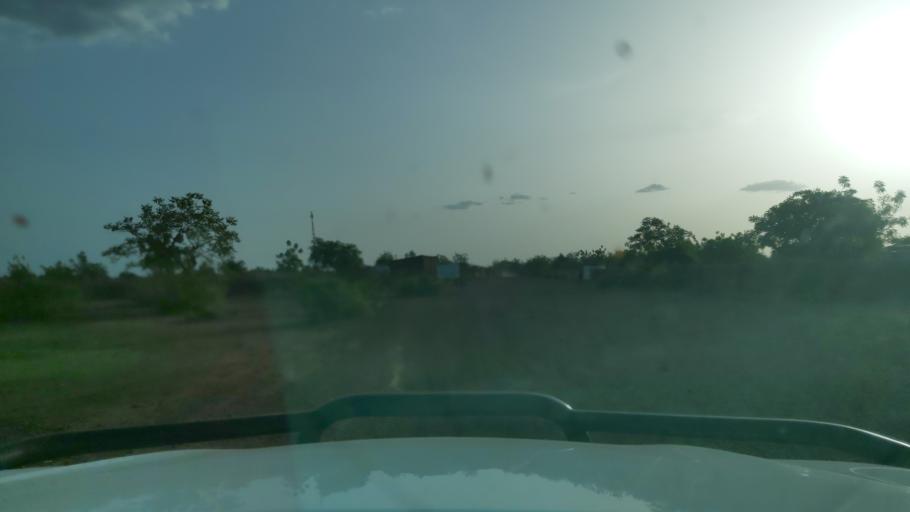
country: ML
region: Koulikoro
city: Kolokani
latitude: 13.2039
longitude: -7.9257
